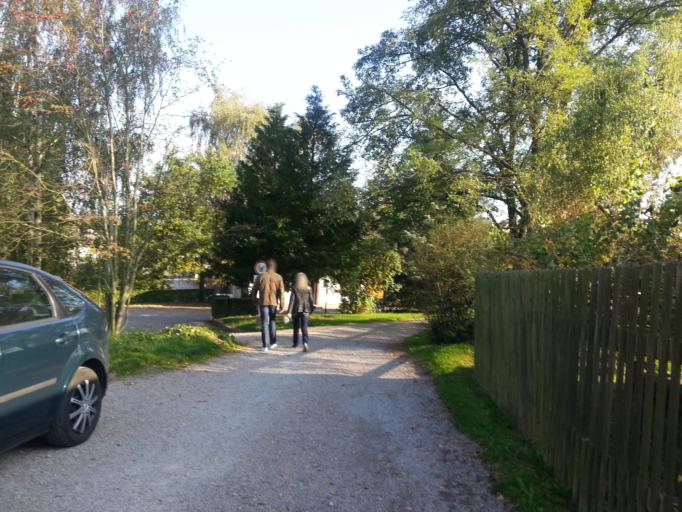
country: DE
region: Saxony
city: Freiberg
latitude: 50.9003
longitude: 13.3337
